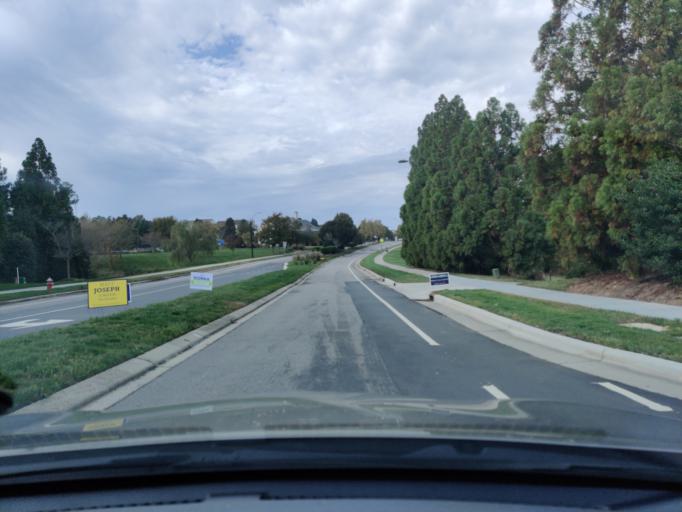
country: US
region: North Carolina
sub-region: Wake County
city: Morrisville
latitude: 35.8406
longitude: -78.8620
